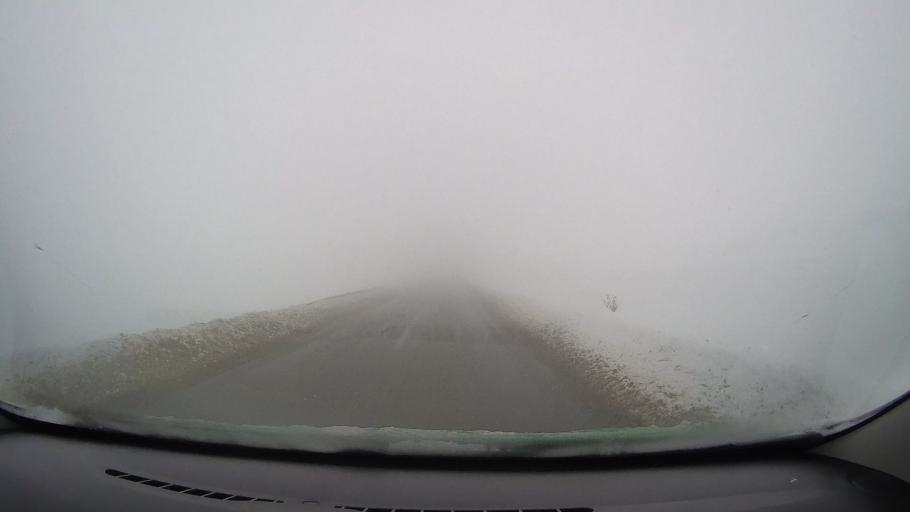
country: RO
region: Sibiu
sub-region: Comuna Poiana Sibiului
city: Poiana Sibiului
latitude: 45.7984
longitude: 23.7075
